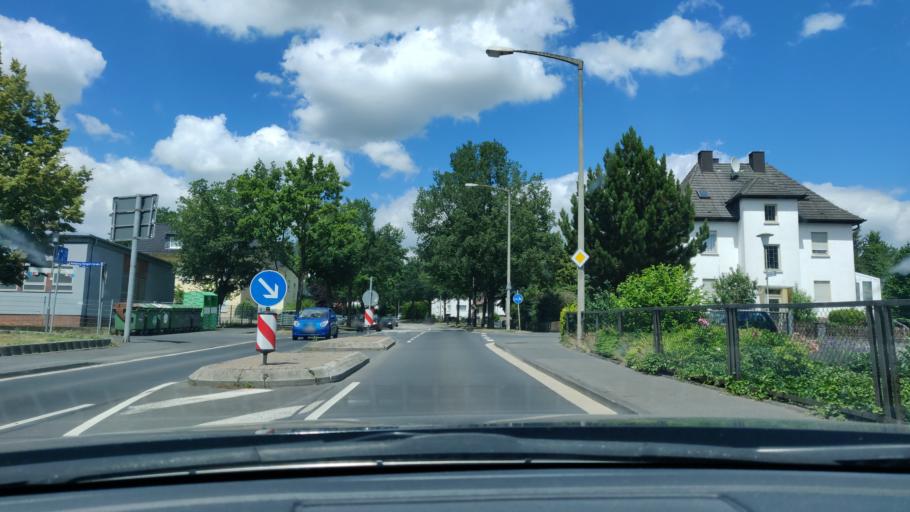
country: DE
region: Hesse
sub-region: Regierungsbezirk Kassel
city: Fuldabruck
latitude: 51.2861
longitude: 9.4529
